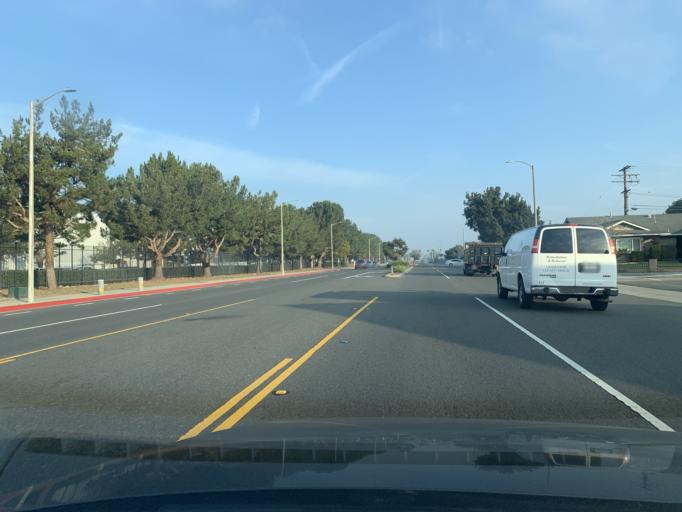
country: US
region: California
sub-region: Orange County
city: Westminster
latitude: 33.7459
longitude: -118.0244
